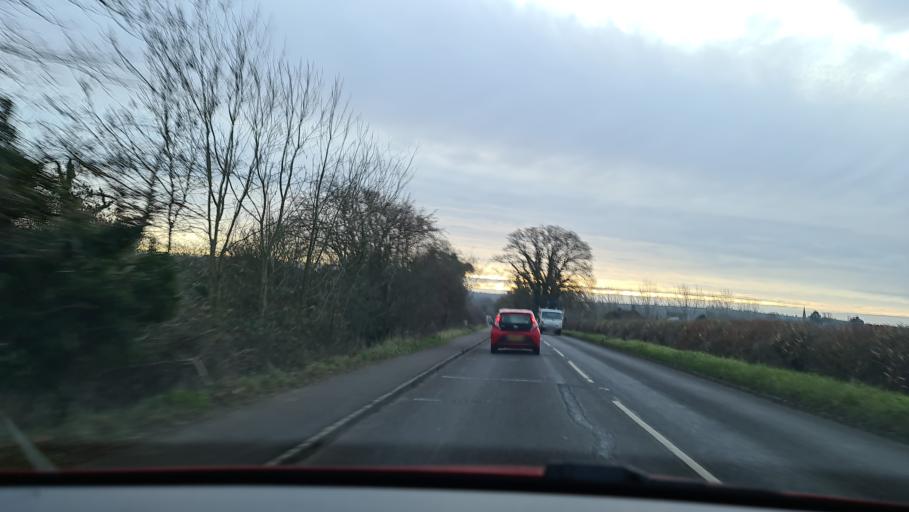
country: GB
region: England
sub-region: Buckinghamshire
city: Princes Risborough
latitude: 51.7317
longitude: -0.8401
